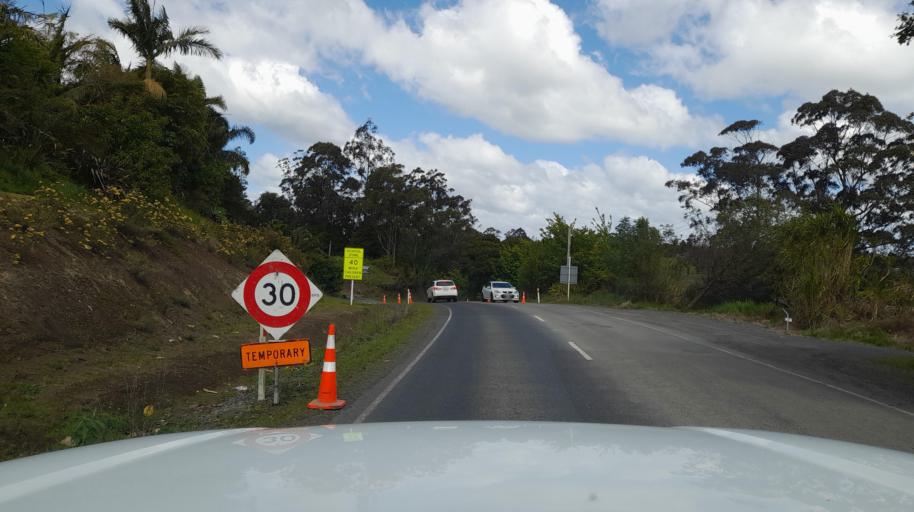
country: NZ
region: Northland
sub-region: Far North District
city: Kerikeri
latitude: -35.2397
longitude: 173.9162
